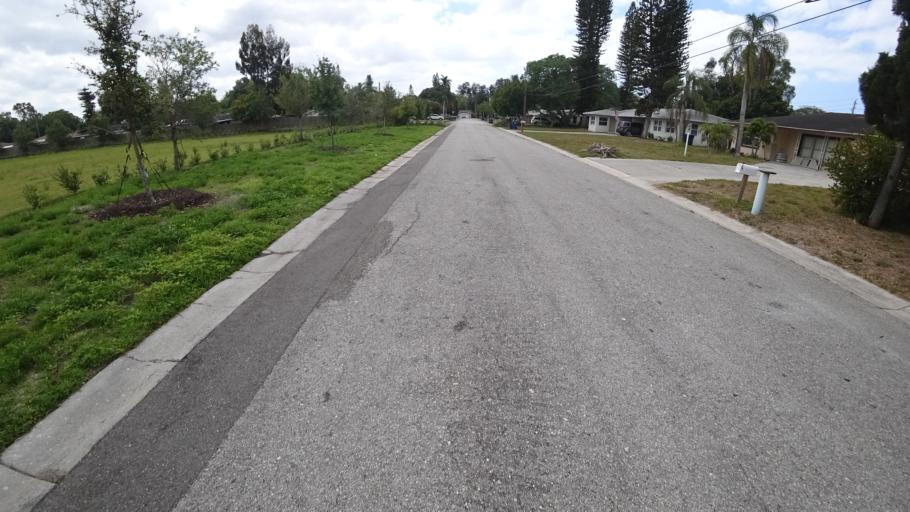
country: US
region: Florida
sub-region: Manatee County
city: South Bradenton
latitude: 27.4457
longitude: -82.5787
